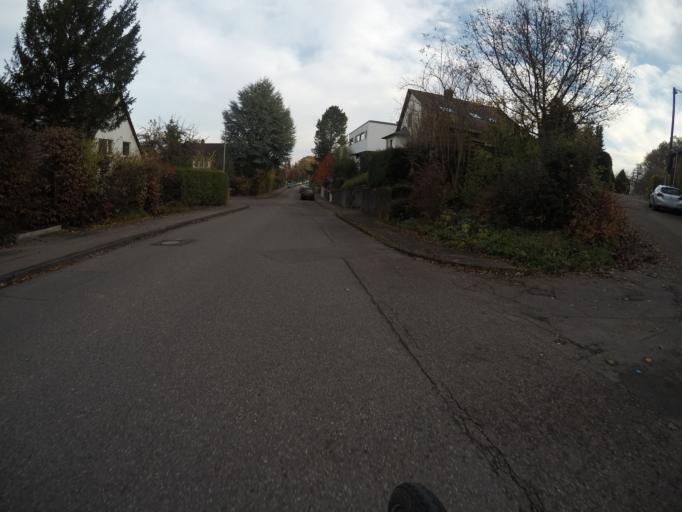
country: DE
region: Baden-Wuerttemberg
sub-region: Regierungsbezirk Stuttgart
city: Steinenbronn
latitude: 48.7030
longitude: 9.1155
